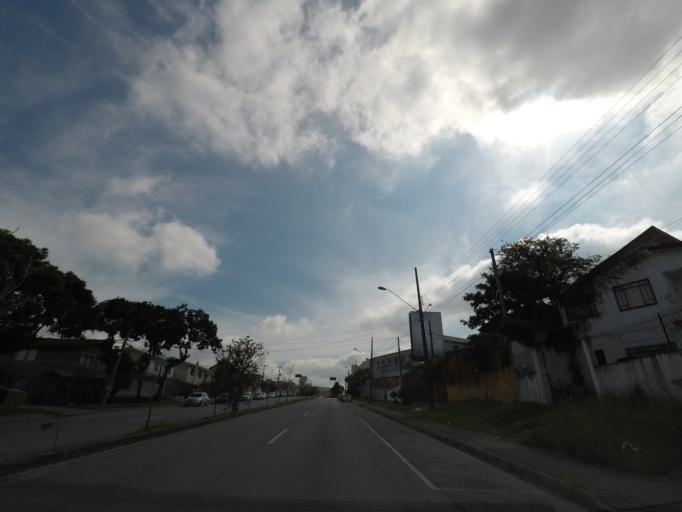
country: BR
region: Parana
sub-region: Curitiba
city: Curitiba
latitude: -25.4785
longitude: -49.2837
